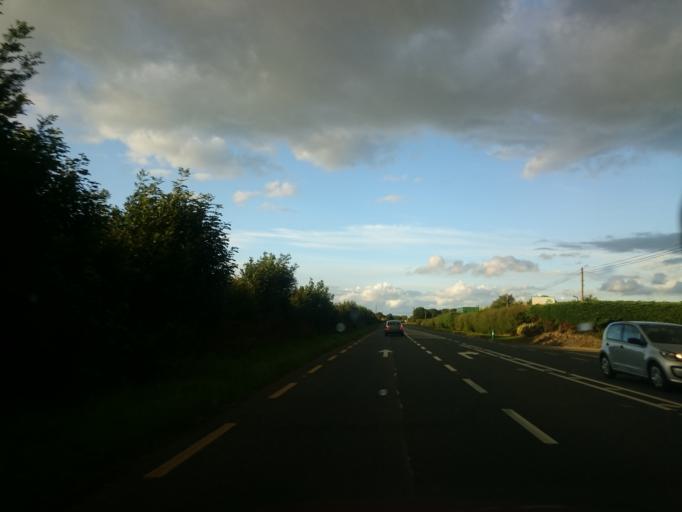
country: IE
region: Leinster
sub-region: Loch Garman
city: Ferns
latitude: 52.6002
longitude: -6.4666
